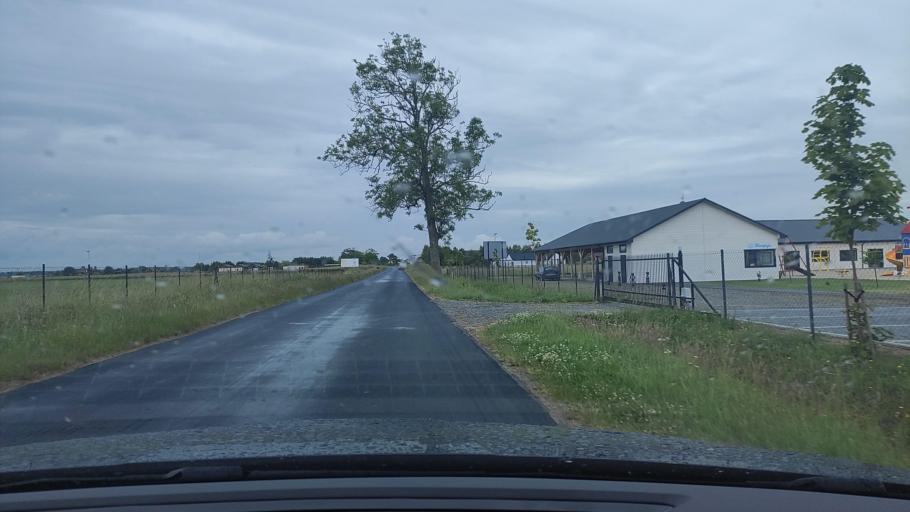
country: PL
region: West Pomeranian Voivodeship
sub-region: Powiat slawienski
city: Slawno
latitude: 54.5308
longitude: 16.5802
